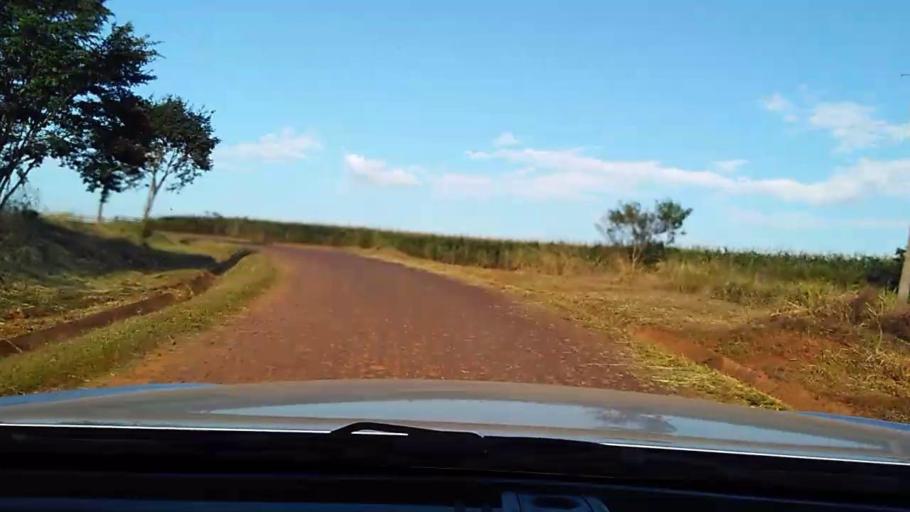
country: PY
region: Alto Parana
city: Doctor Juan Leon Mallorquin
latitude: -25.7069
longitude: -55.3894
